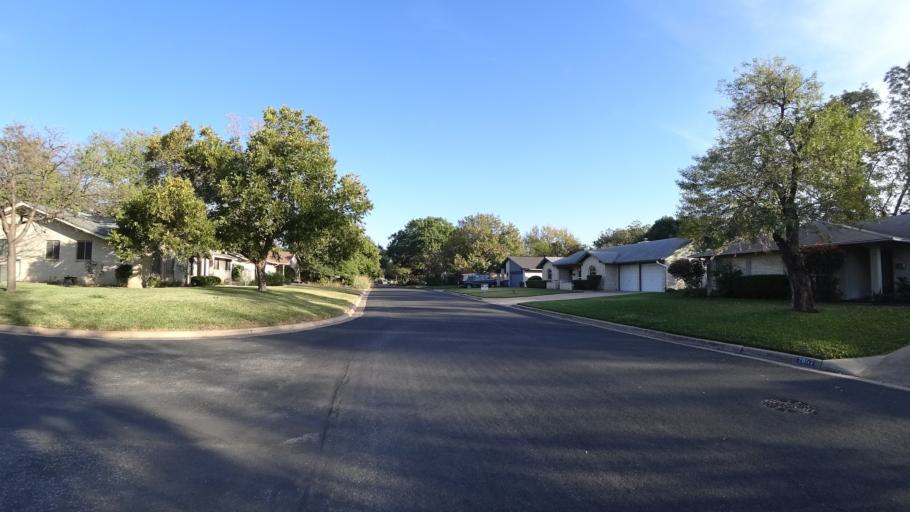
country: US
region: Texas
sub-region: Williamson County
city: Jollyville
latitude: 30.3706
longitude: -97.7333
